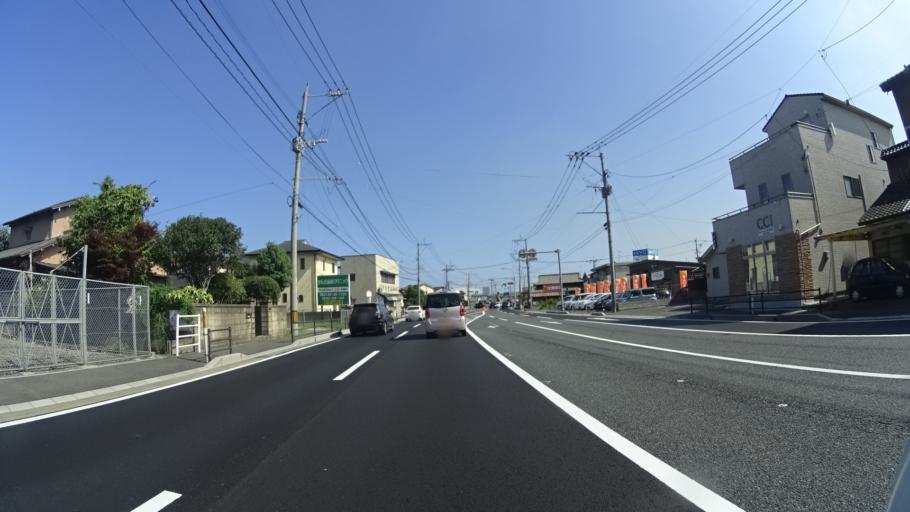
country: JP
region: Fukuoka
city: Kanda
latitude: 33.7955
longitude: 130.9788
